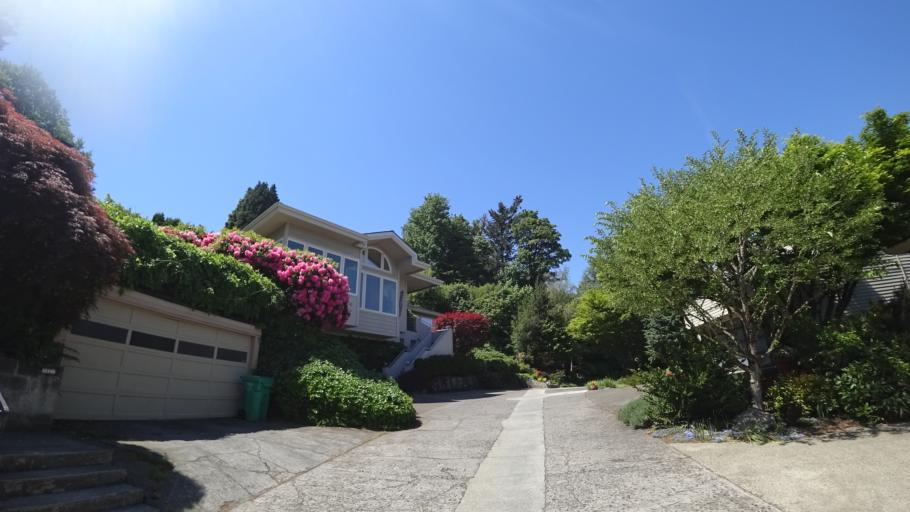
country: US
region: Oregon
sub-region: Multnomah County
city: Portland
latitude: 45.4831
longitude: -122.6850
